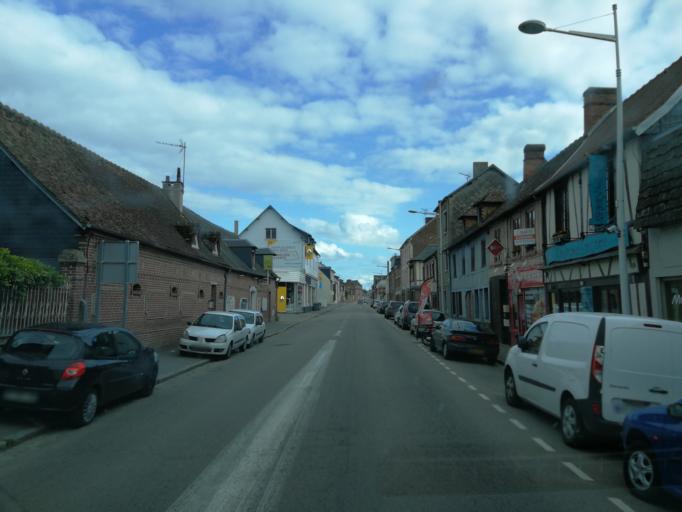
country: FR
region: Haute-Normandie
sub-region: Departement de l'Eure
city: Le Neubourg
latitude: 49.1474
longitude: 0.9012
